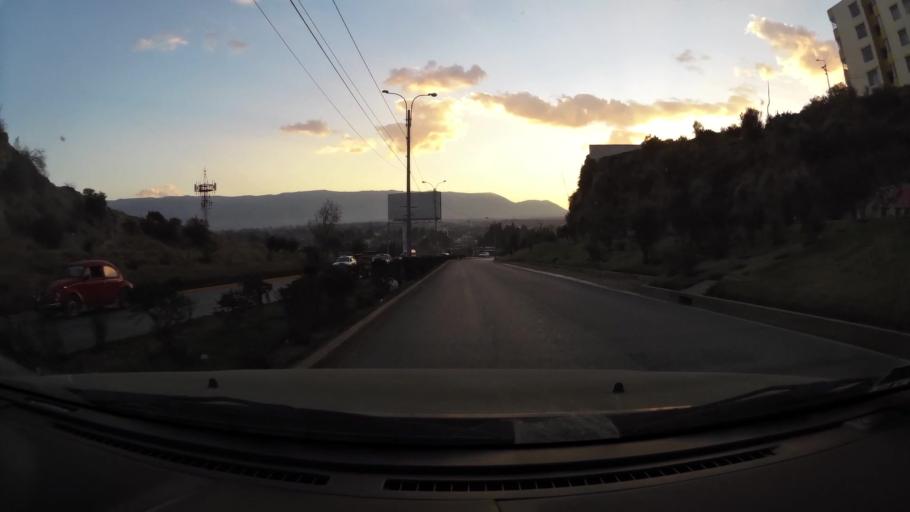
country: PE
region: Junin
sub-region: Provincia de Huancayo
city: Pilcomay
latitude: -12.0532
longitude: -75.2367
